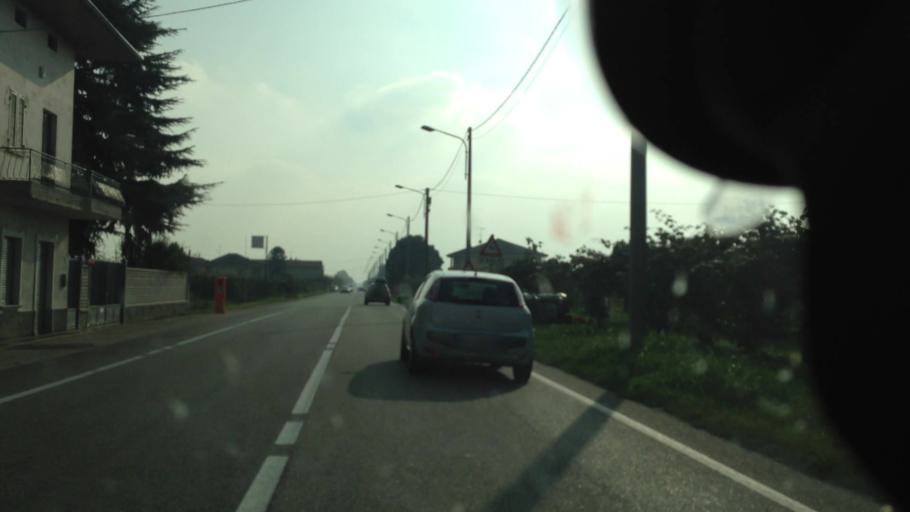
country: IT
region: Piedmont
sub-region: Provincia di Vercelli
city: Borgo d'Ale
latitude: 45.3438
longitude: 8.0486
